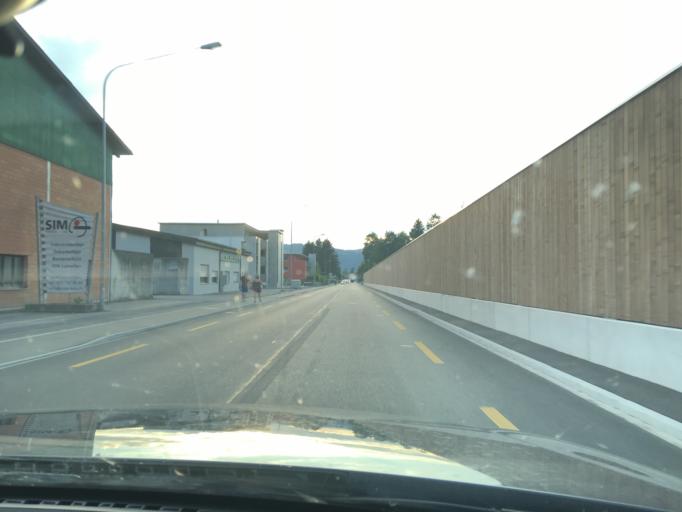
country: CH
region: Saint Gallen
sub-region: Wahlkreis Rheintal
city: Diepoldsau
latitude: 47.3793
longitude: 9.6676
